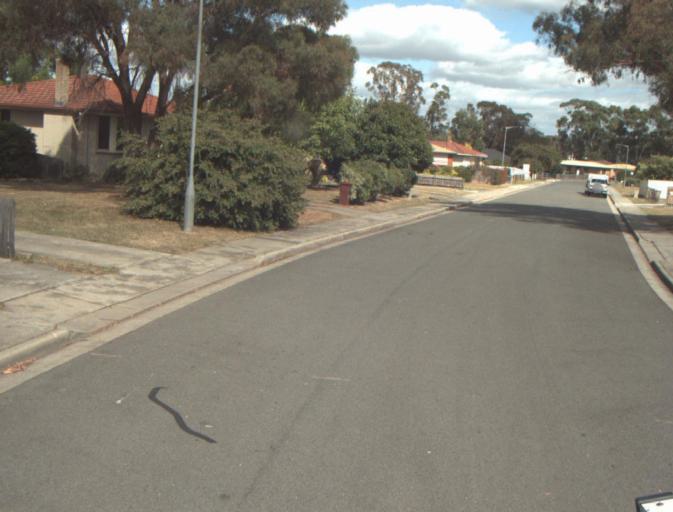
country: AU
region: Tasmania
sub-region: Launceston
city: Newstead
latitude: -41.4172
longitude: 147.1816
